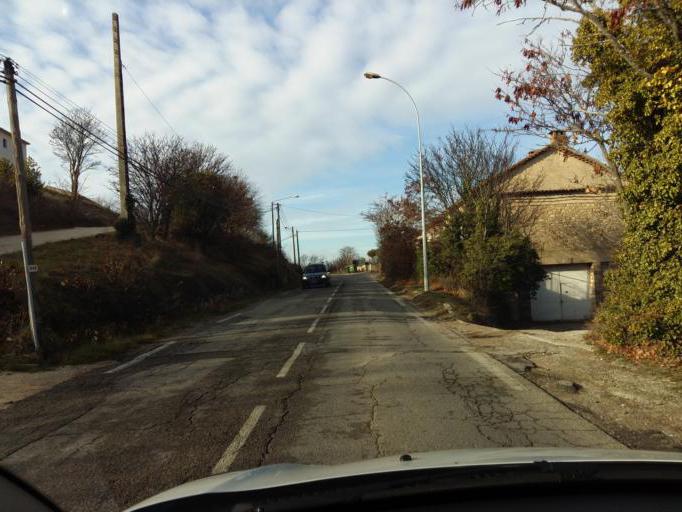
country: FR
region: Provence-Alpes-Cote d'Azur
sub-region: Departement du Vaucluse
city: Apt
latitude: 43.8769
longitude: 5.3798
